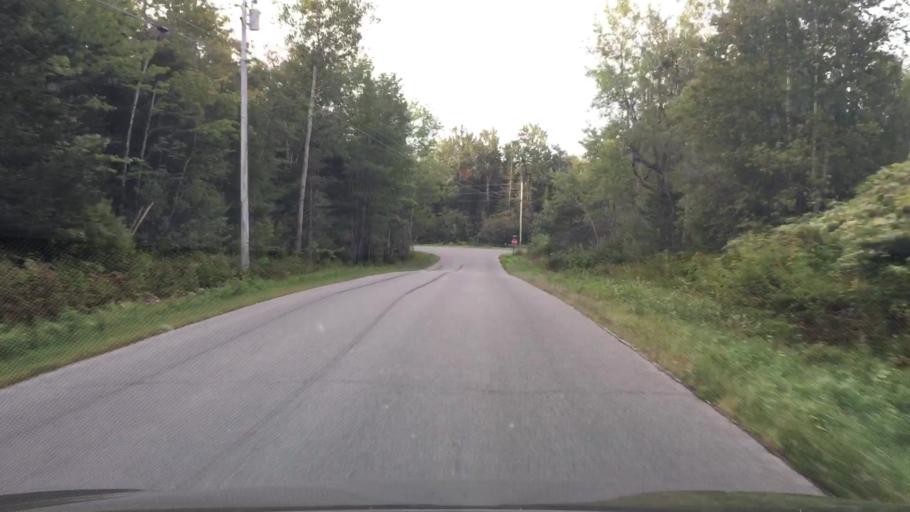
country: US
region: Maine
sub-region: Waldo County
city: Stockton Springs
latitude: 44.4952
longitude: -68.8741
